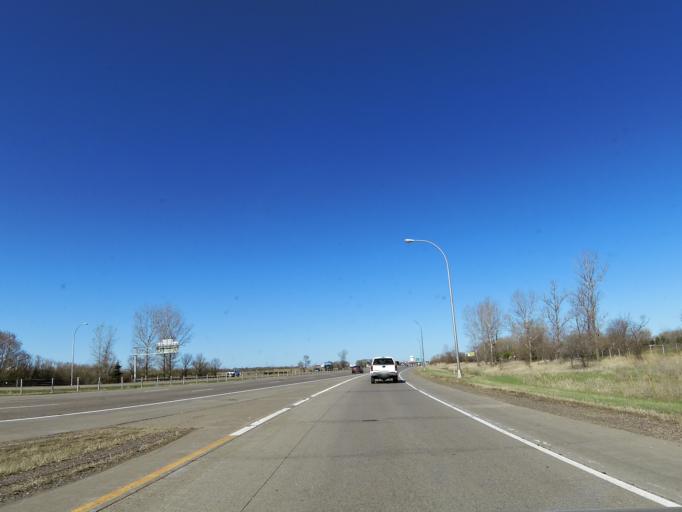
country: US
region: Minnesota
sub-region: Washington County
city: Lake Elmo
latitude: 44.9490
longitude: -92.8671
